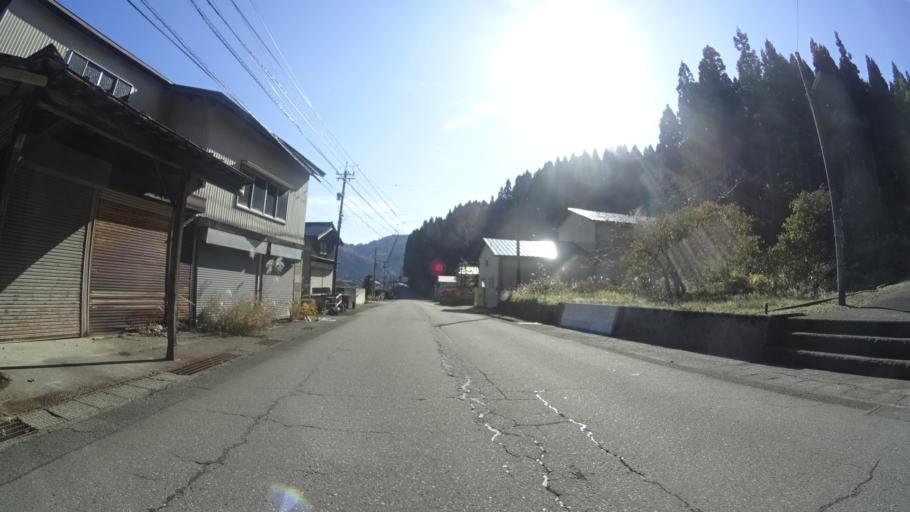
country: JP
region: Ishikawa
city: Tsurugi-asahimachi
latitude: 36.3641
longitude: 136.5926
